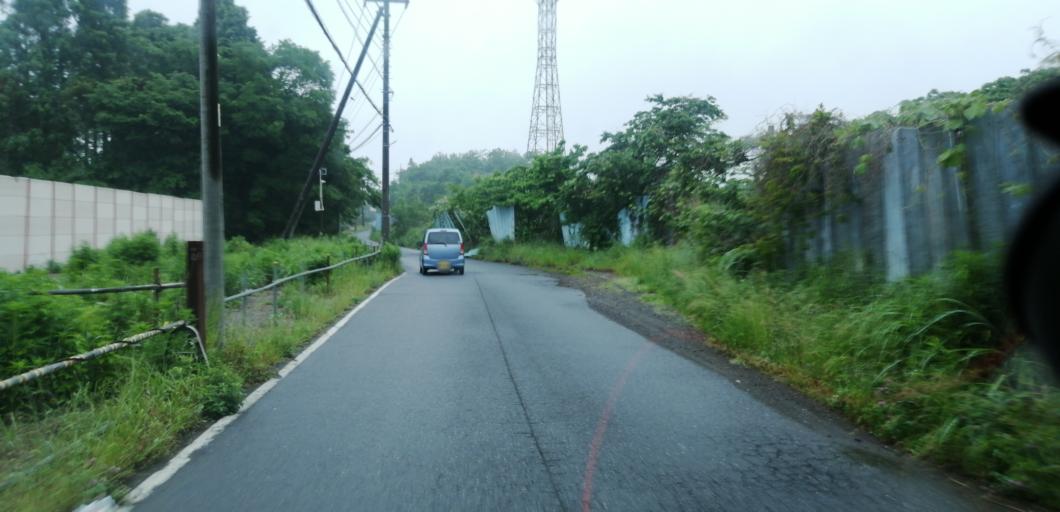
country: JP
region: Chiba
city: Ichihara
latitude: 35.4757
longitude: 140.1497
